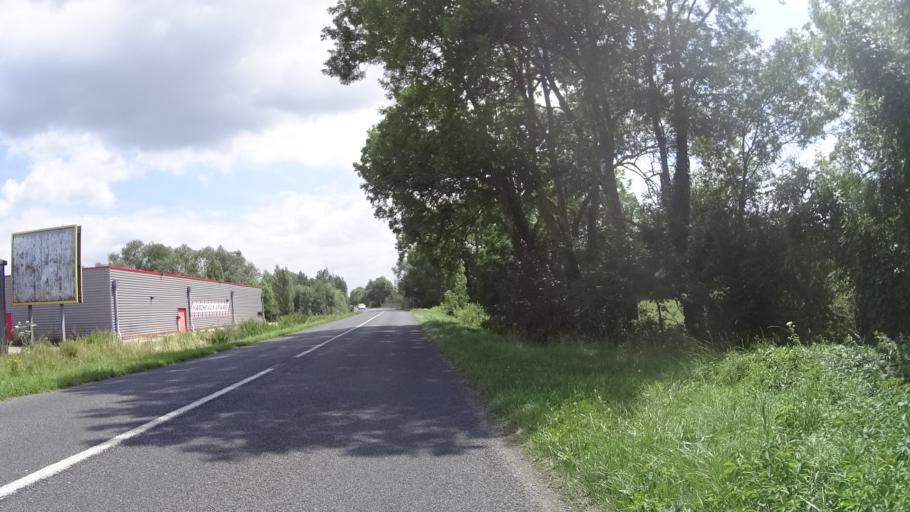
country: FR
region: Lorraine
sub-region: Departement de la Meuse
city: Vignot
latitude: 48.7585
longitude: 5.6064
